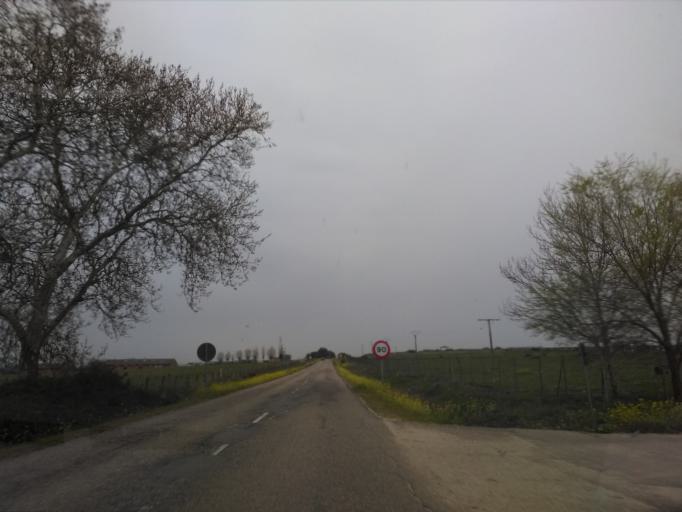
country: ES
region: Castille and Leon
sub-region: Provincia de Salamanca
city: Vitigudino
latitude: 41.0000
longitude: -6.4422
